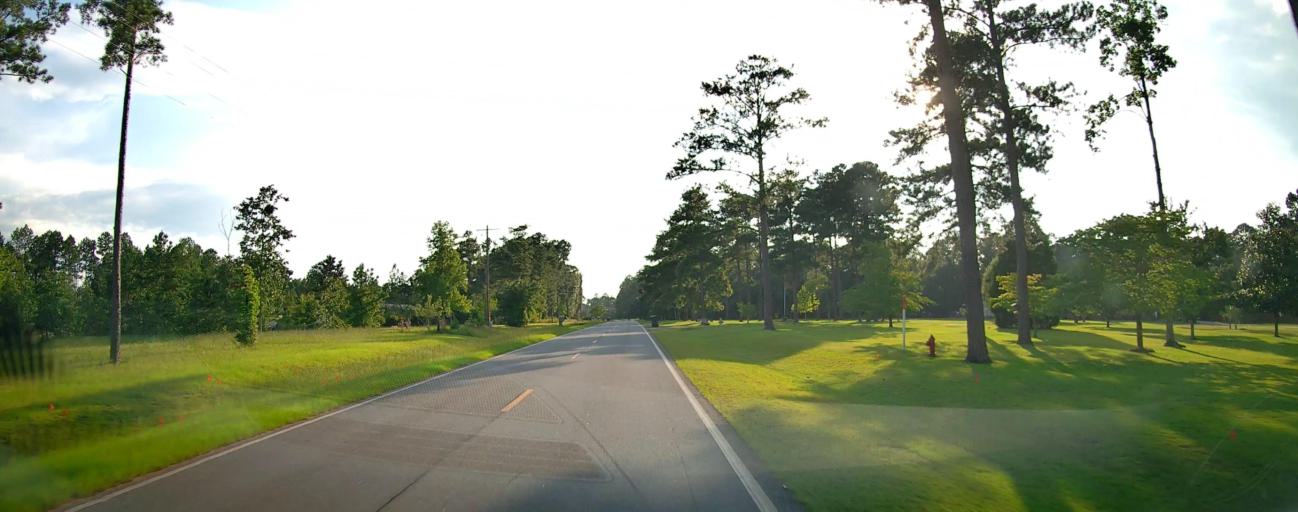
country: US
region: Georgia
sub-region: Peach County
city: Byron
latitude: 32.7051
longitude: -83.8128
